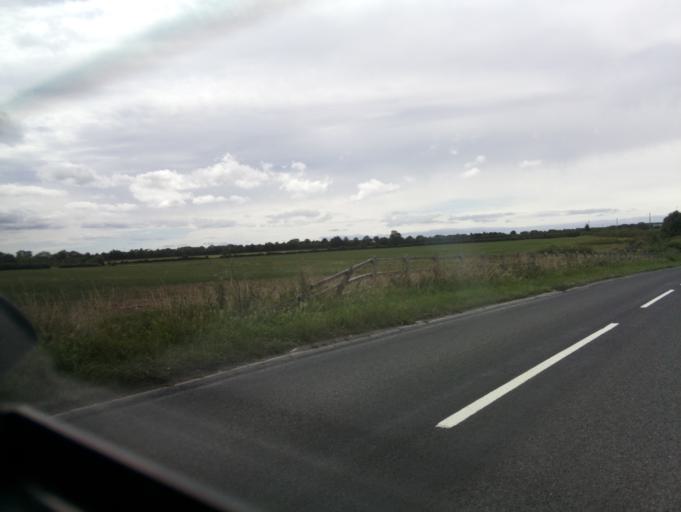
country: GB
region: England
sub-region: Somerset
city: Ilchester
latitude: 51.0447
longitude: -2.6545
